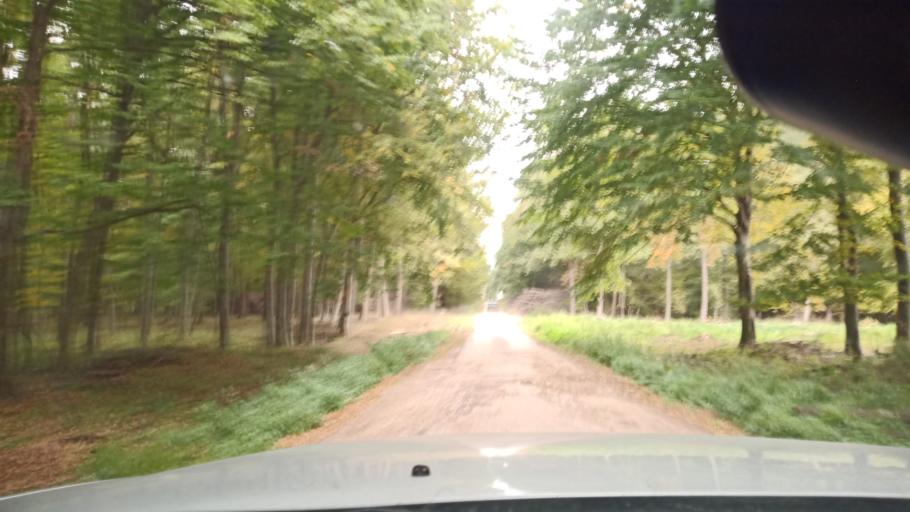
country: HU
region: Fejer
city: Pusztavam
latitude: 47.3900
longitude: 18.2894
